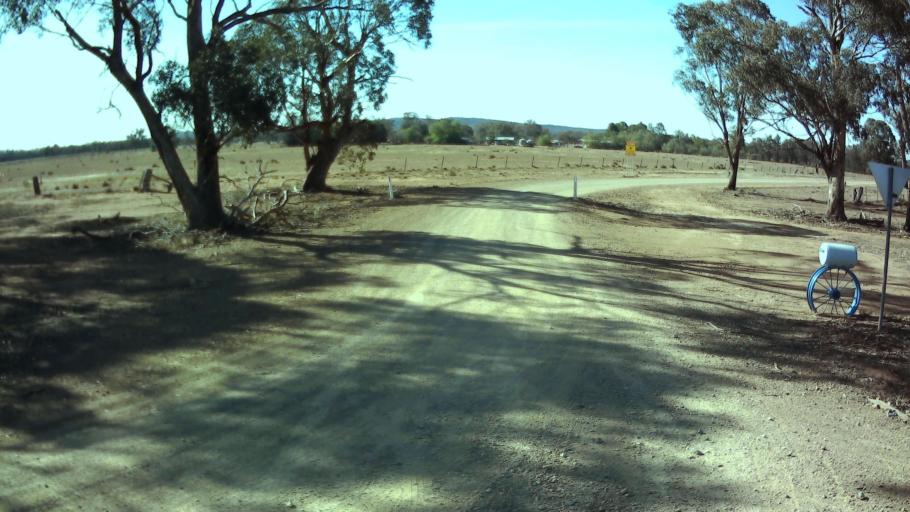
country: AU
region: New South Wales
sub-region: Weddin
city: Grenfell
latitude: -33.8510
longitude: 147.8755
